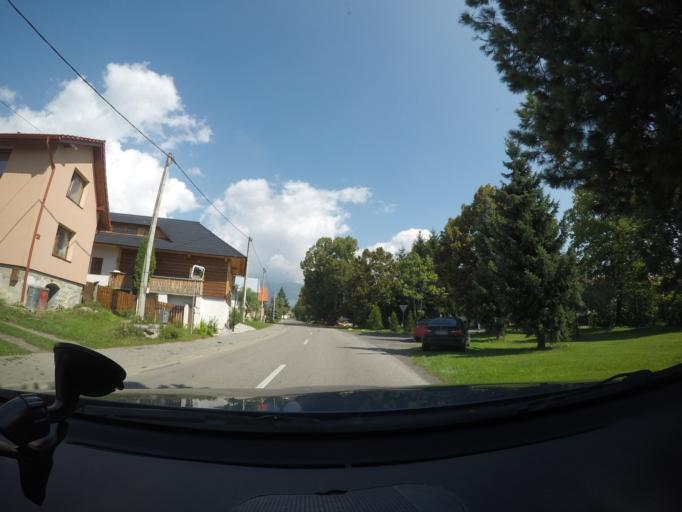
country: SK
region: Zilinsky
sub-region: Okres Liptovsky Mikulas
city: Liptovsky Mikulas
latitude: 49.1210
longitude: 19.6128
